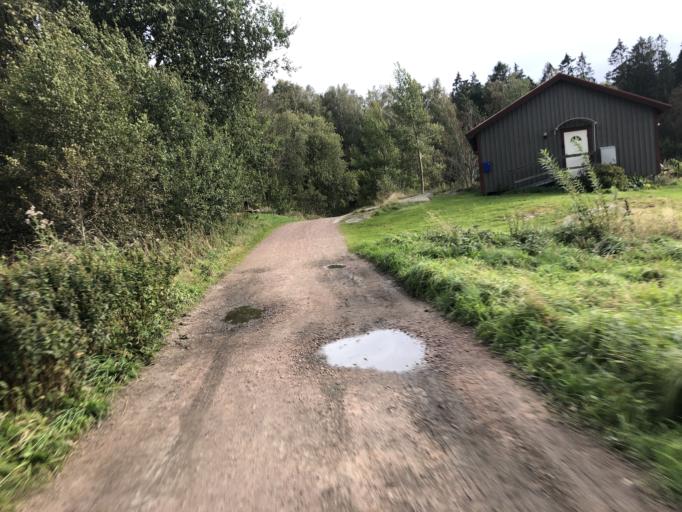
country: SE
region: Vaestra Goetaland
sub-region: Goteborg
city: Majorna
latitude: 57.7497
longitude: 11.9008
